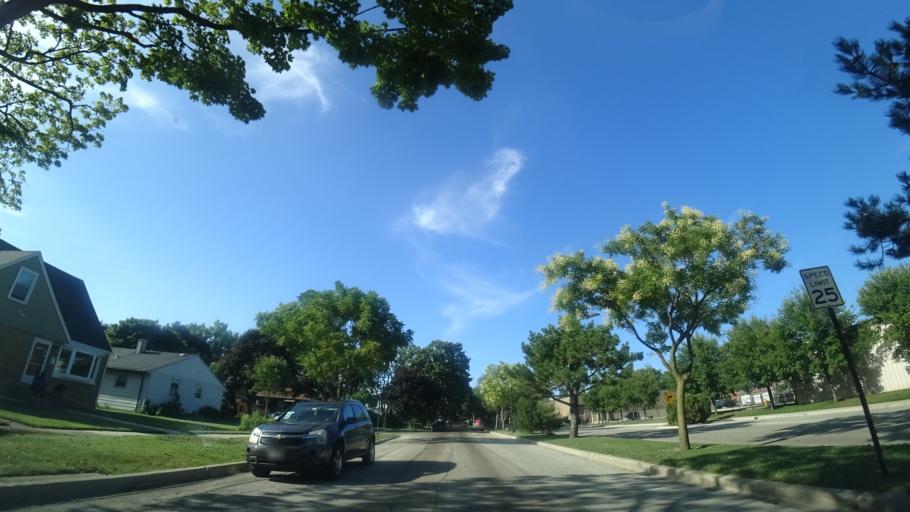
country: US
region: Illinois
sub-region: Cook County
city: Evanston
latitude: 42.0359
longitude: -87.7054
